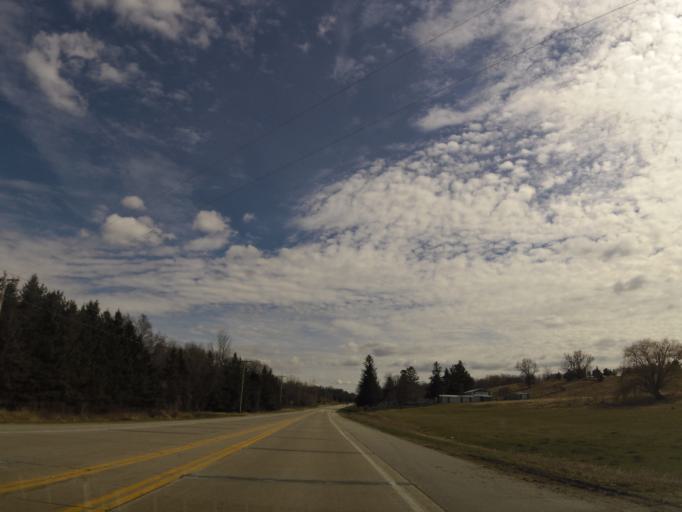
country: US
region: Minnesota
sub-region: Olmsted County
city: Rochester
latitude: 43.9712
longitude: -92.4373
